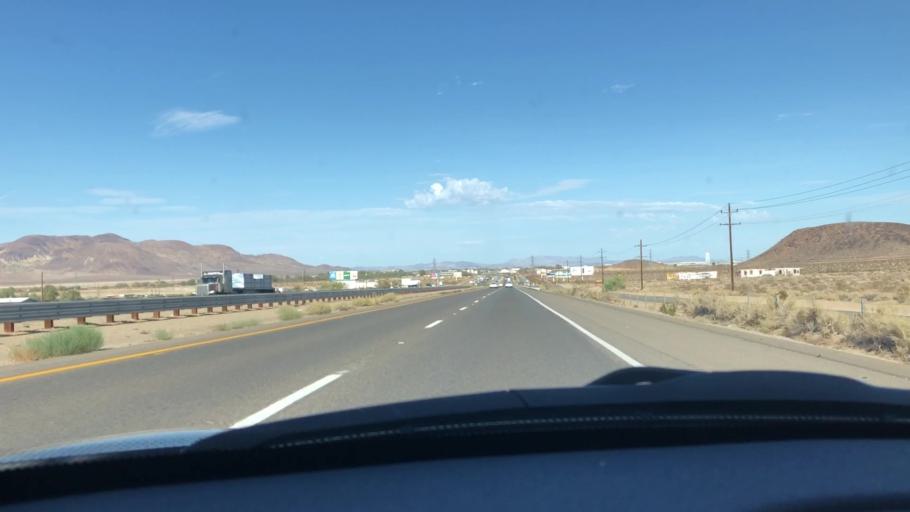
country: US
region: California
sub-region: San Bernardino County
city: Barstow
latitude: 34.9012
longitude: -116.9137
